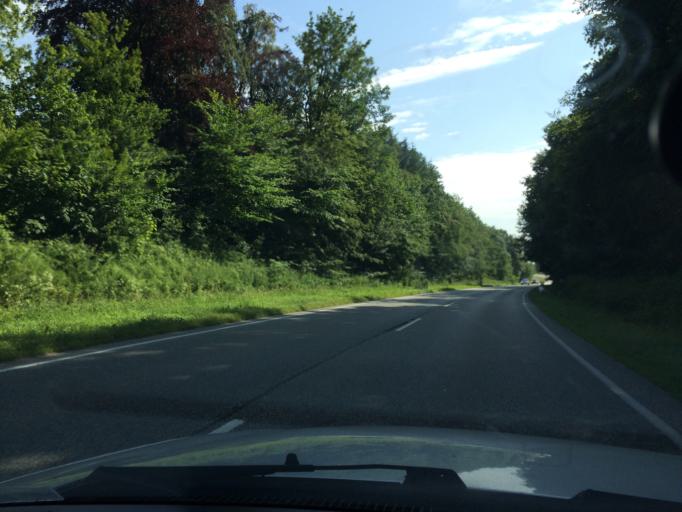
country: DE
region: Schleswig-Holstein
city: Oeversee
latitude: 54.7161
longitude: 9.4434
